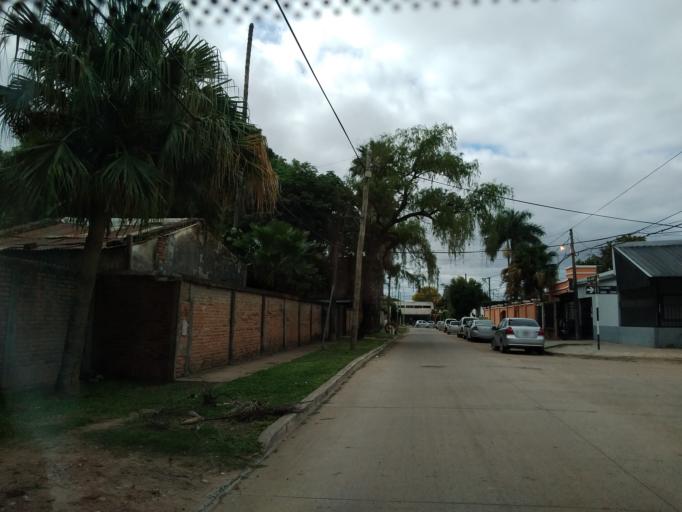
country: AR
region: Corrientes
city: Corrientes
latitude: -27.4734
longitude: -58.8086
